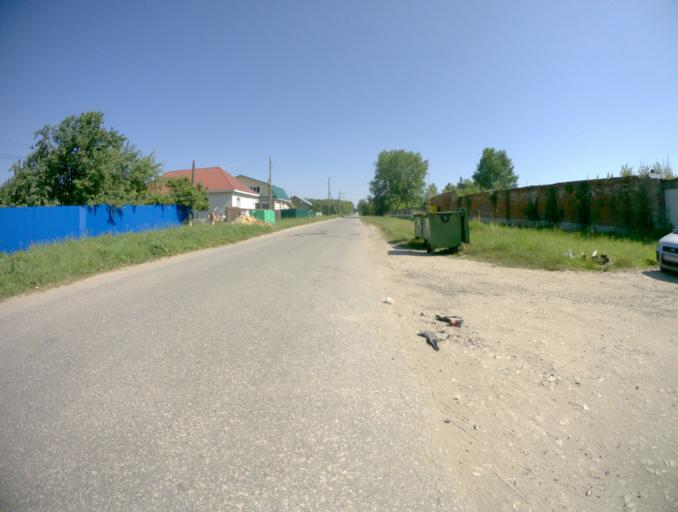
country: RU
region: Vladimir
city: Vyazniki
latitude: 56.2329
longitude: 42.1943
